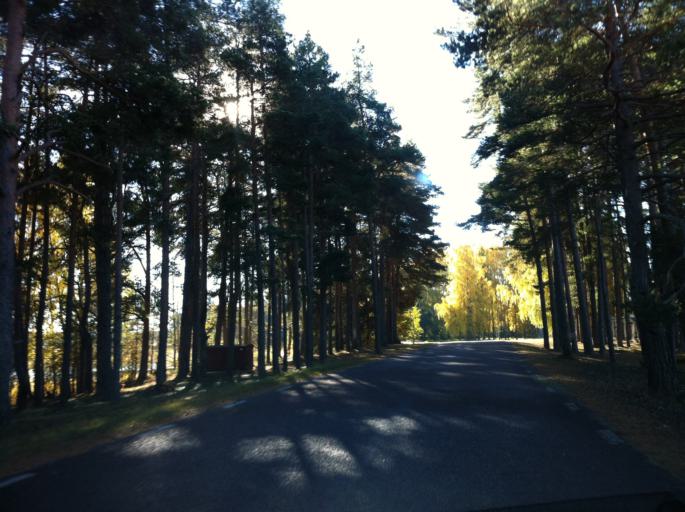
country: SE
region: Gaevleborg
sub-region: Gavle Kommun
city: Hedesunda
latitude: 60.3362
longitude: 17.0227
